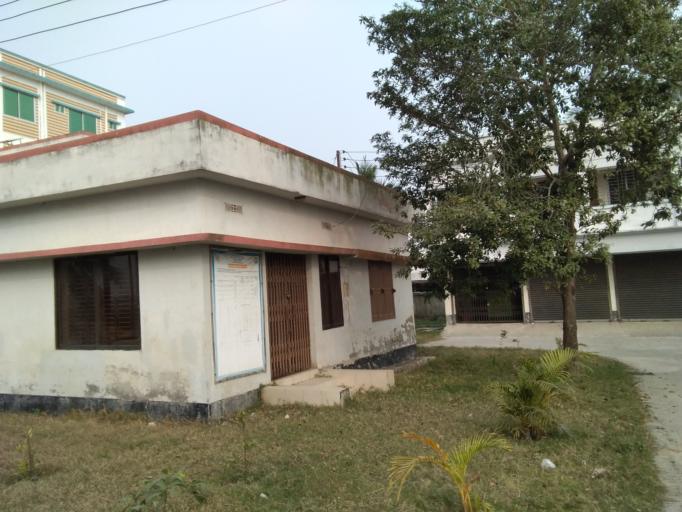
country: BD
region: Khulna
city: Satkhira
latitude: 22.6733
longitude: 89.0785
